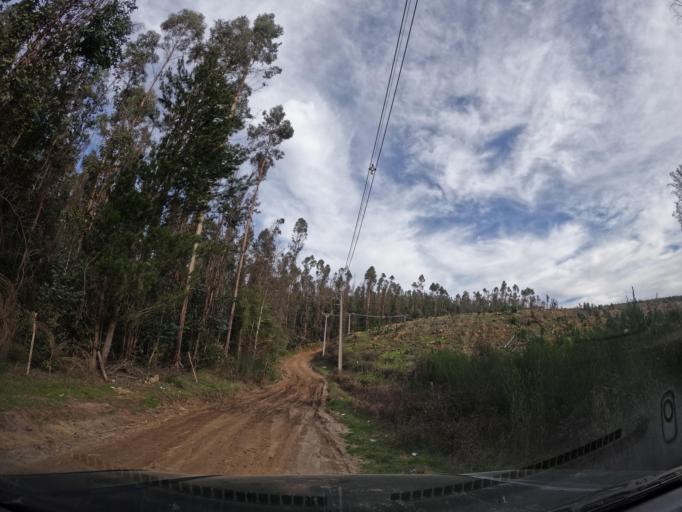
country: CL
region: Biobio
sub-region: Provincia de Concepcion
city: Chiguayante
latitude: -37.0199
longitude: -72.9144
